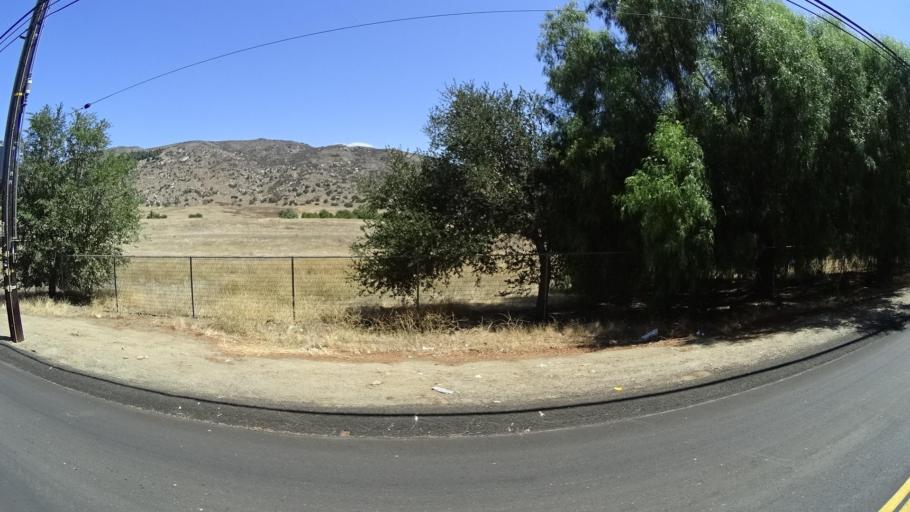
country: US
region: California
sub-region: San Diego County
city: Rainbow
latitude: 33.3471
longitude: -117.1356
